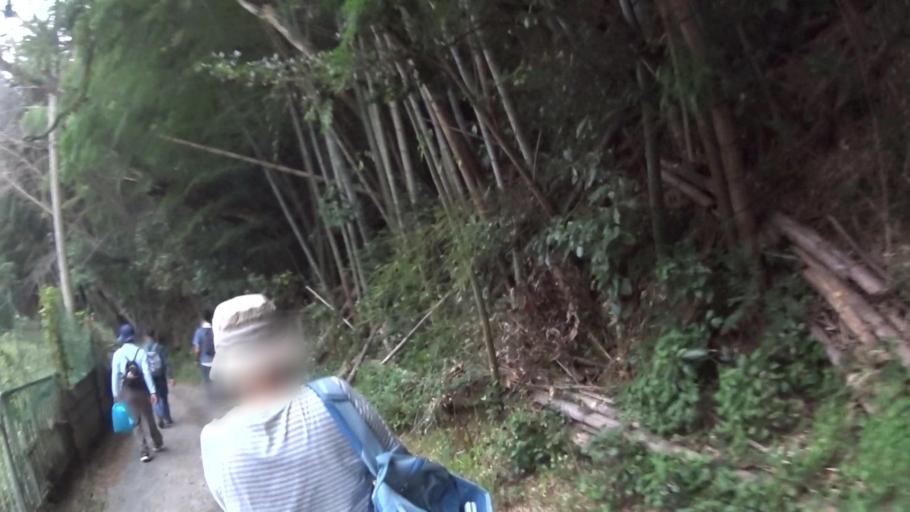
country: JP
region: Osaka
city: Kaizuka
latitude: 34.4618
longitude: 135.2944
